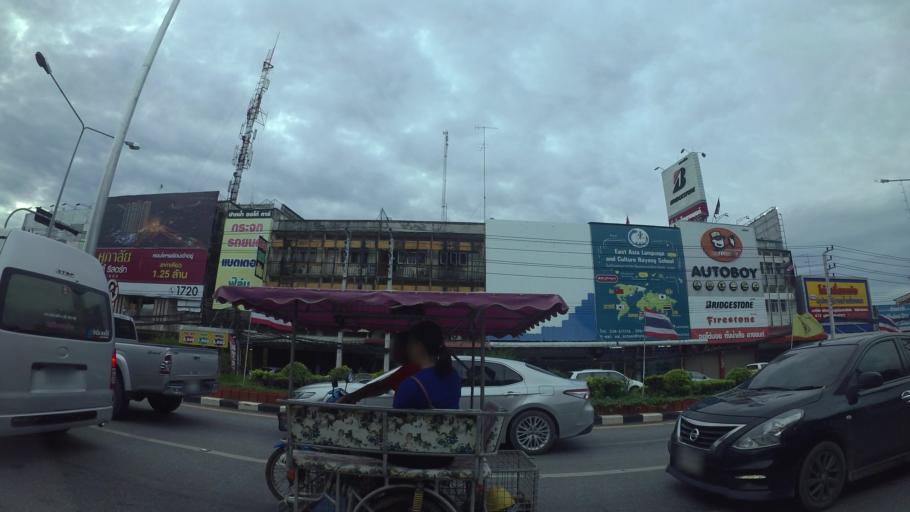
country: TH
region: Rayong
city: Rayong
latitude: 12.6829
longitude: 101.2658
